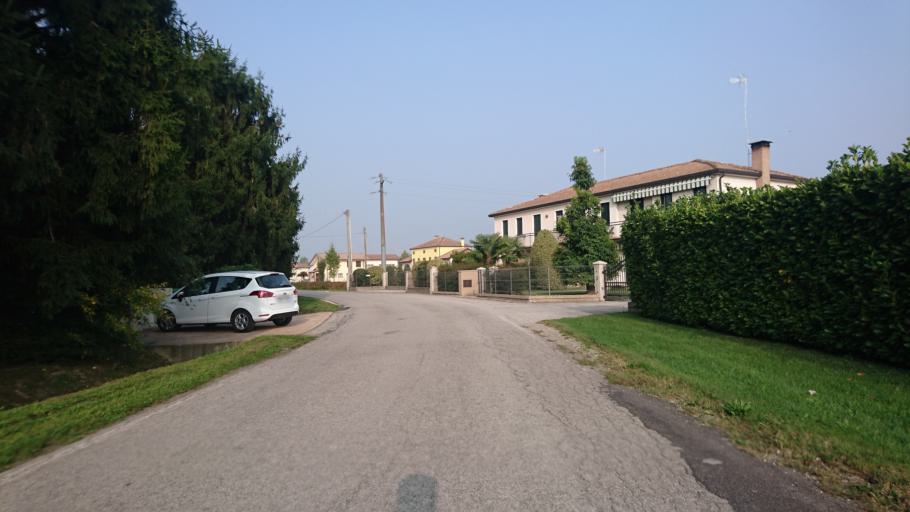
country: IT
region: Veneto
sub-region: Provincia di Padova
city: Santa Maria di Non
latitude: 45.5077
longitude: 11.8487
